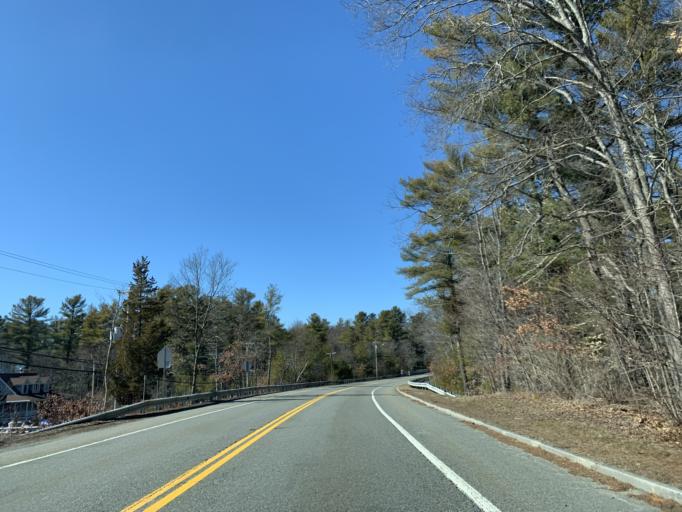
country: US
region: Massachusetts
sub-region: Bristol County
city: Norton
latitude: 41.9461
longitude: -71.1749
